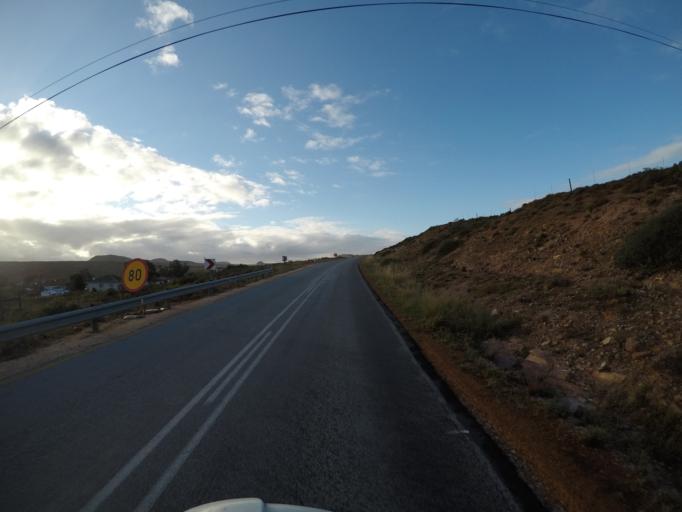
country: ZA
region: Western Cape
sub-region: West Coast District Municipality
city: Clanwilliam
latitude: -32.3281
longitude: 18.3696
